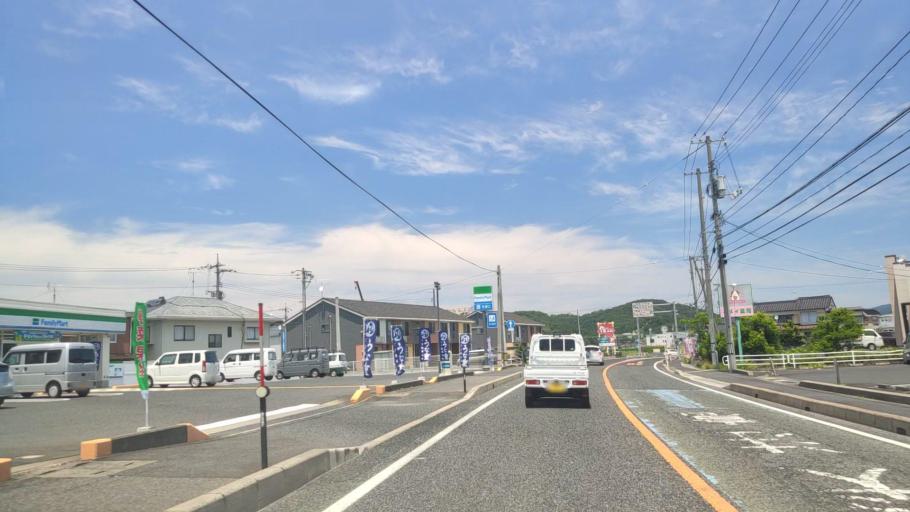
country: JP
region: Tottori
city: Tottori
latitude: 35.4164
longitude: 134.2562
